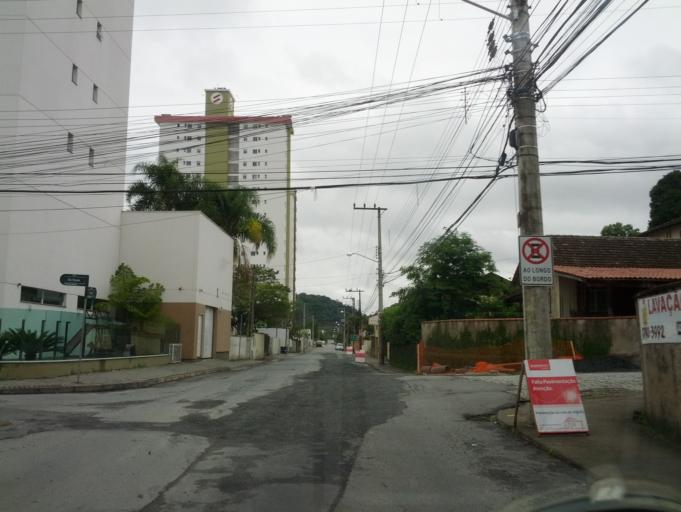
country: BR
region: Santa Catarina
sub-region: Blumenau
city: Blumenau
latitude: -26.8880
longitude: -49.0677
